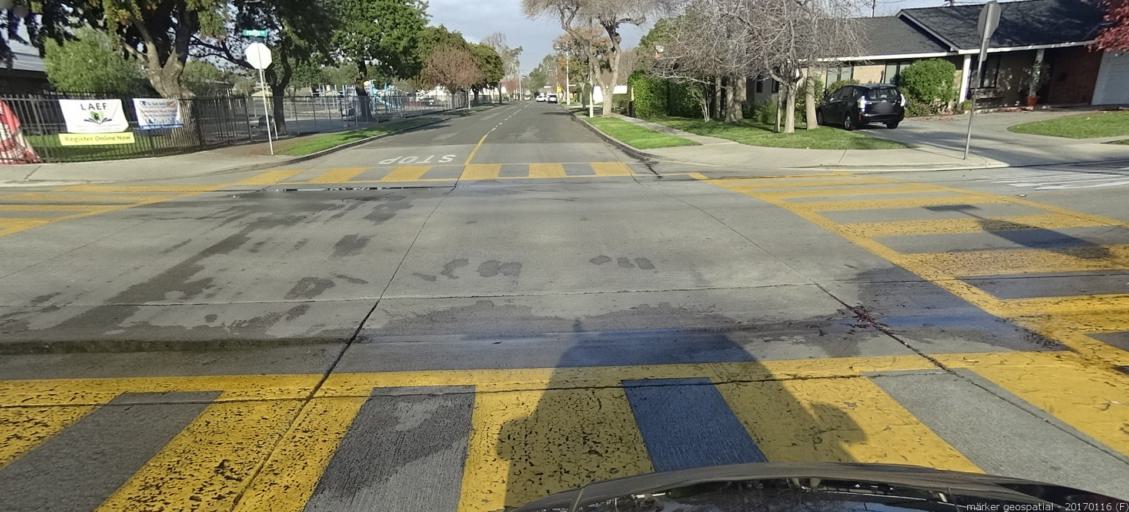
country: US
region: California
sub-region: Orange County
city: Los Alamitos
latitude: 33.7967
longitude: -118.0811
